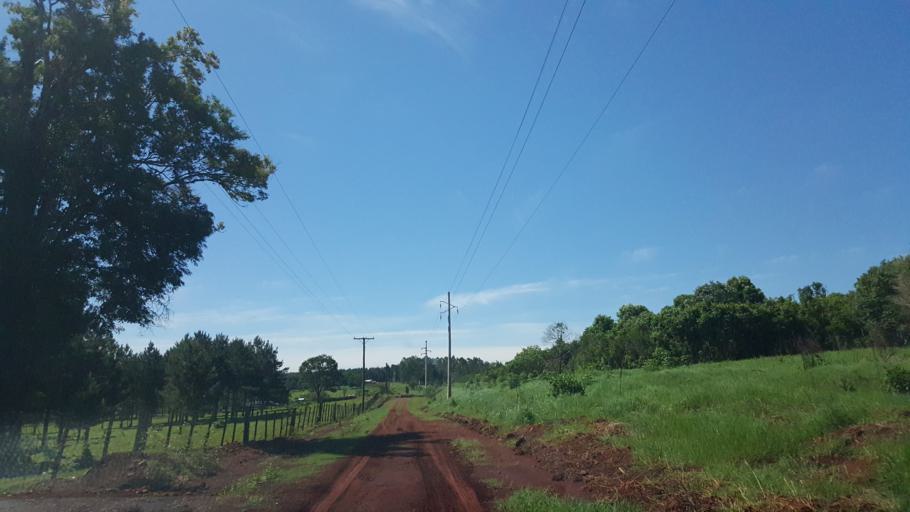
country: AR
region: Misiones
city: Capiovi
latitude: -26.9227
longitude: -55.0719
